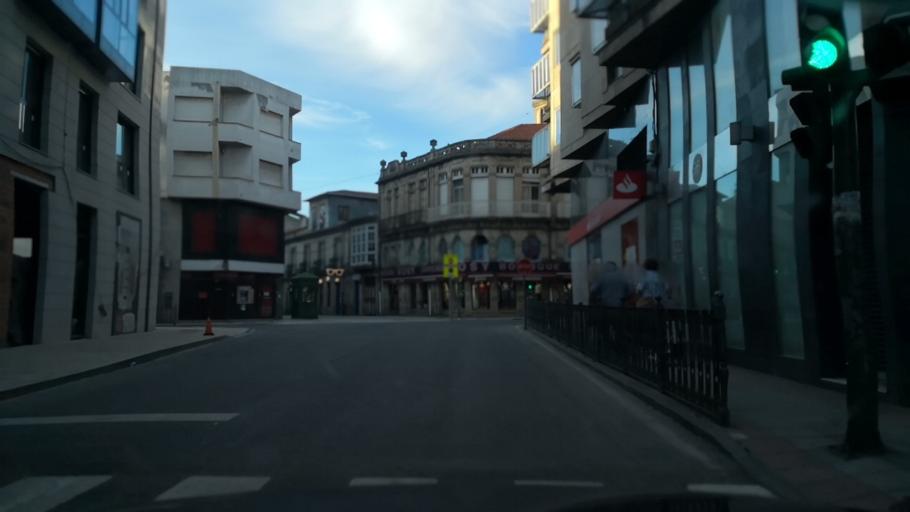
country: ES
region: Galicia
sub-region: Provincia de Ourense
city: Verin
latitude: 41.9399
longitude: -7.4376
